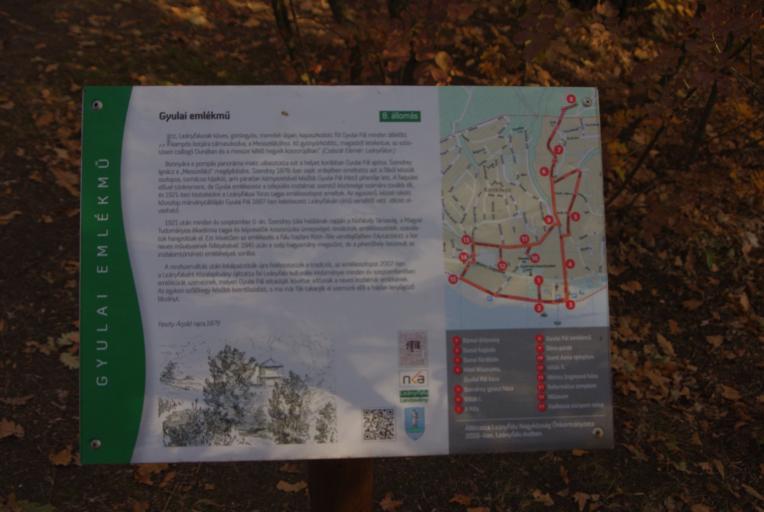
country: HU
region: Pest
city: Leanyfalu
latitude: 47.7203
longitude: 19.0744
